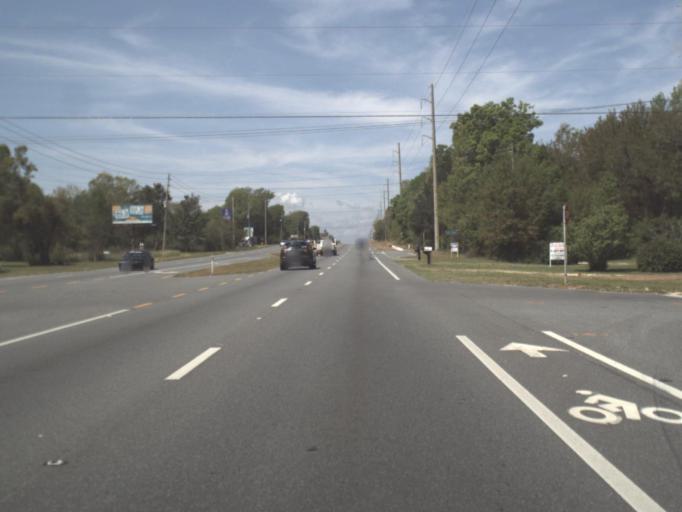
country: US
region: Florida
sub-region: Santa Rosa County
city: Pace
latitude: 30.6030
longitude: -87.0982
